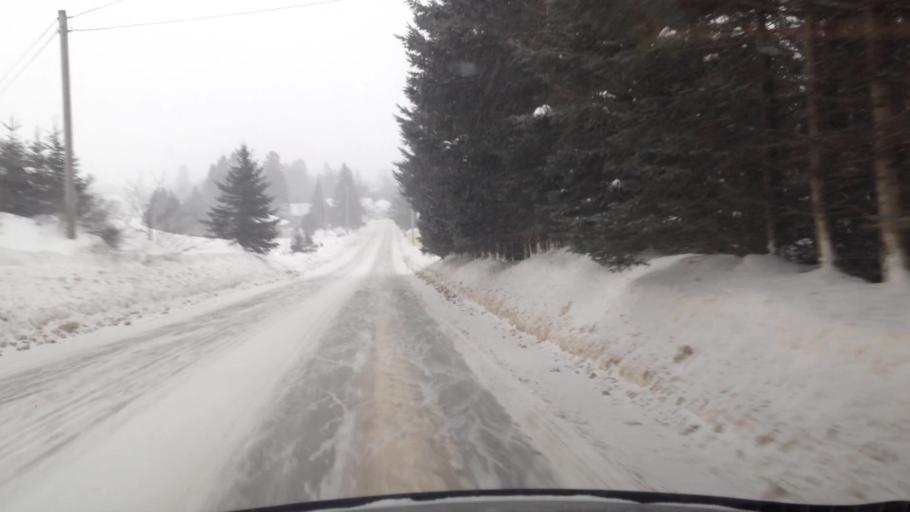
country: CA
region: Quebec
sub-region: Laurentides
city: Mont-Tremblant
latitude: 45.9674
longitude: -74.6215
